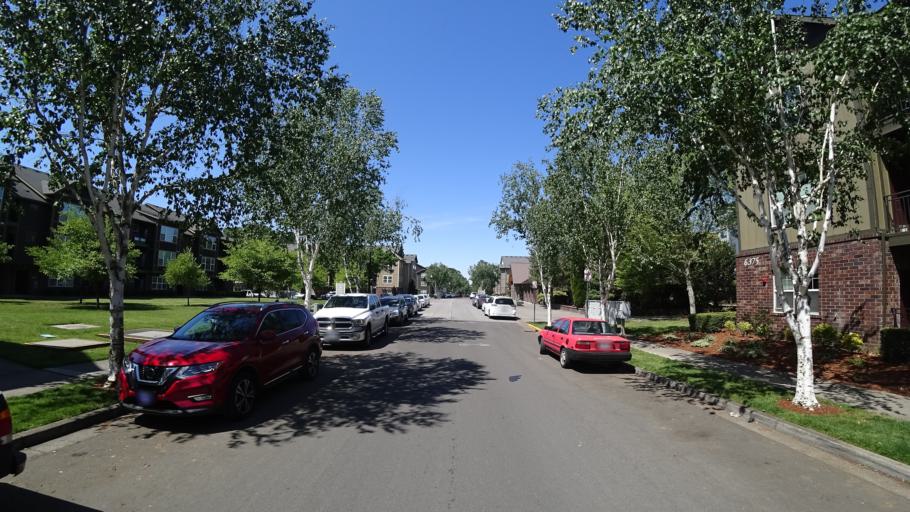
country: US
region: Oregon
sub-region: Washington County
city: Rockcreek
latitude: 45.5298
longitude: -122.9162
